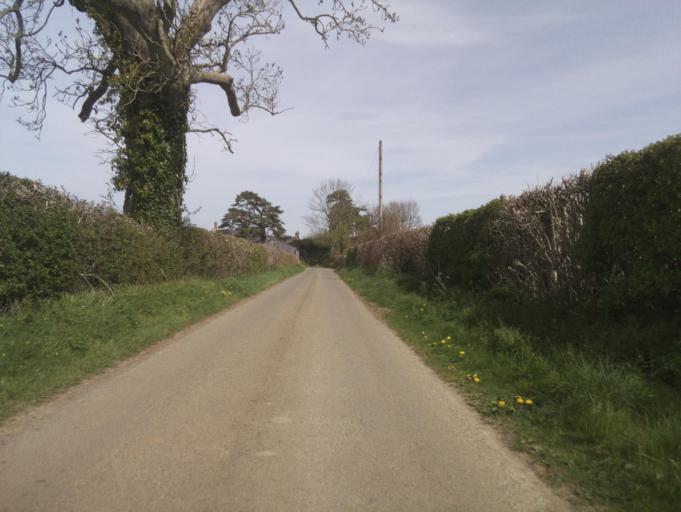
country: GB
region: England
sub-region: Dorset
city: Sherborne
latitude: 50.9941
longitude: -2.5438
